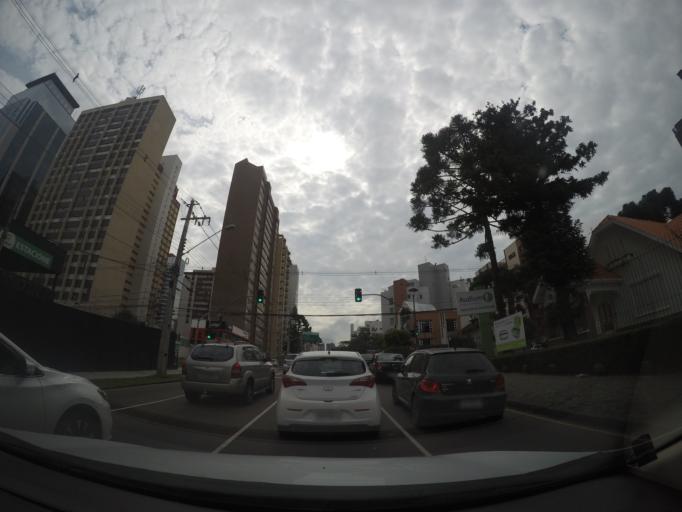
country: BR
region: Parana
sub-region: Curitiba
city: Curitiba
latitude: -25.4185
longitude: -49.2624
